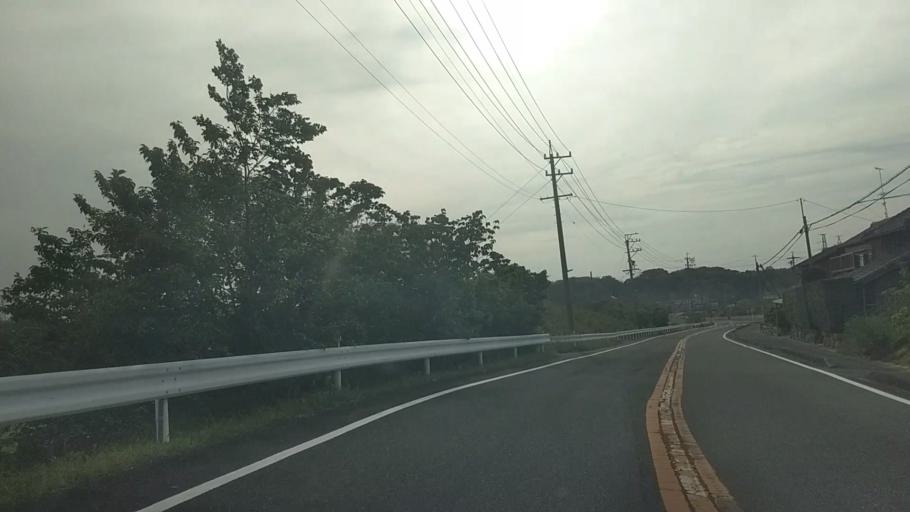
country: JP
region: Shizuoka
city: Kosai-shi
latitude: 34.7463
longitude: 137.6086
